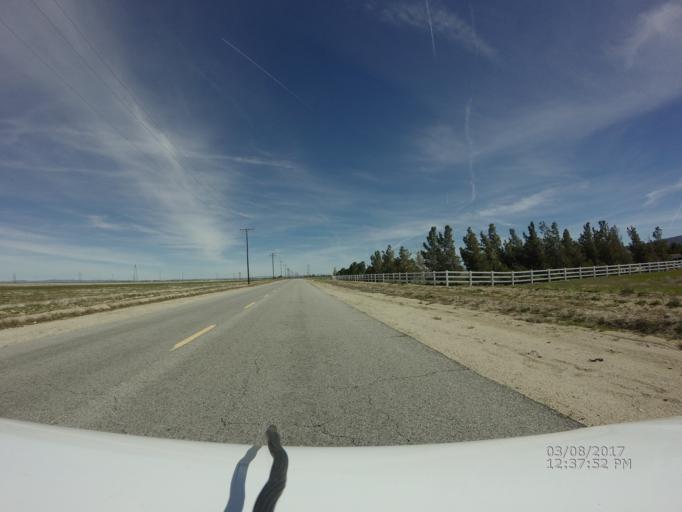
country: US
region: California
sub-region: Los Angeles County
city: Leona Valley
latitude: 34.7038
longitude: -118.3301
